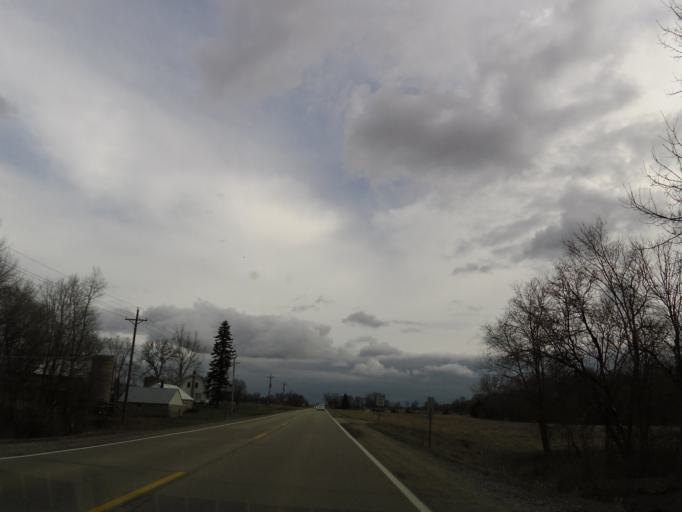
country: US
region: Iowa
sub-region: Black Hawk County
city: Elk Run Heights
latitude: 42.4614
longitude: -92.2197
